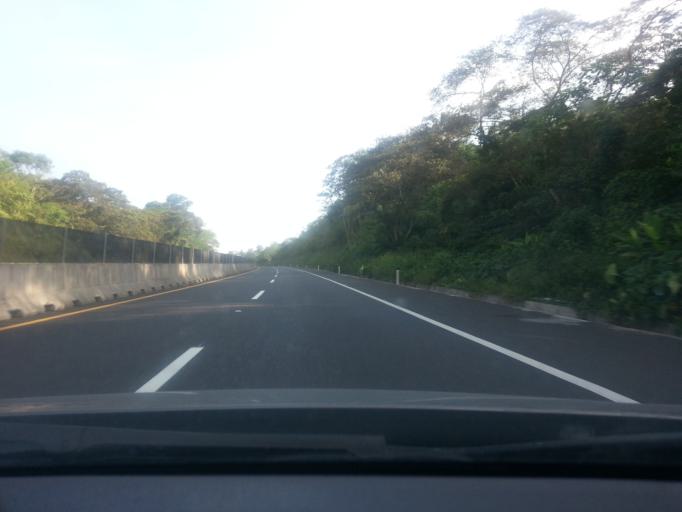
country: MX
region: Puebla
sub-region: Xicotepec
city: San Lorenzo
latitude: 20.4020
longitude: -97.9432
